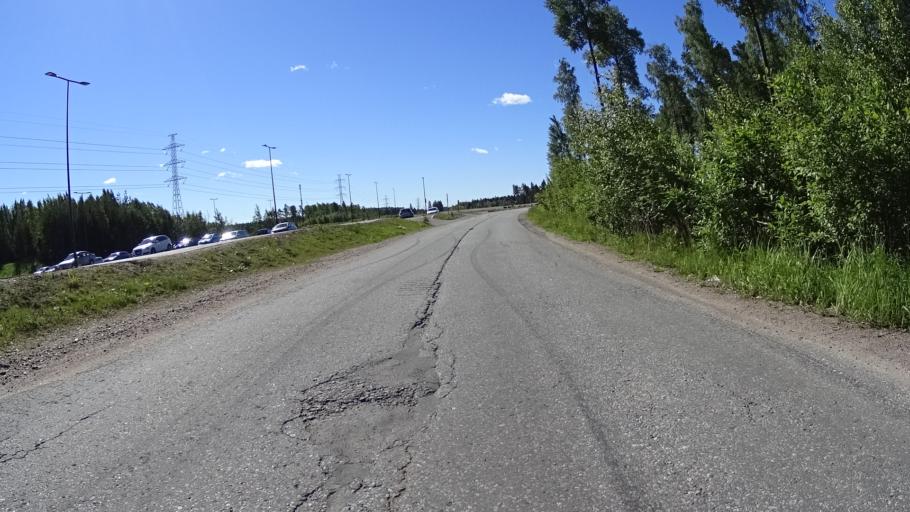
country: FI
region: Uusimaa
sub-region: Helsinki
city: Kilo
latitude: 60.3128
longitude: 24.8379
